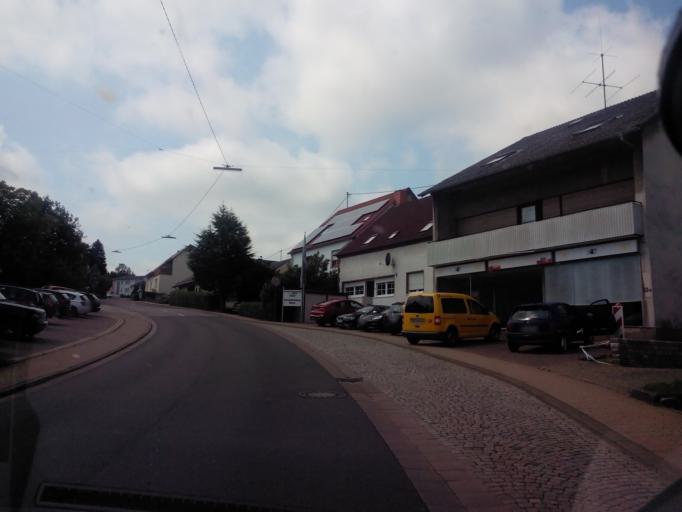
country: DE
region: Saarland
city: Eppelborn
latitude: 49.3882
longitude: 6.9970
